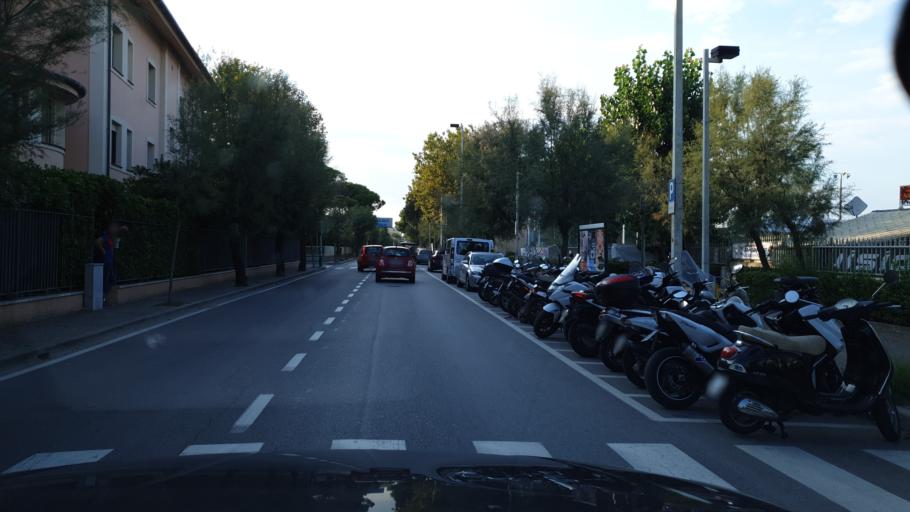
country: IT
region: Emilia-Romagna
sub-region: Provincia di Rimini
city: Riccione
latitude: 43.9934
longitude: 12.6751
